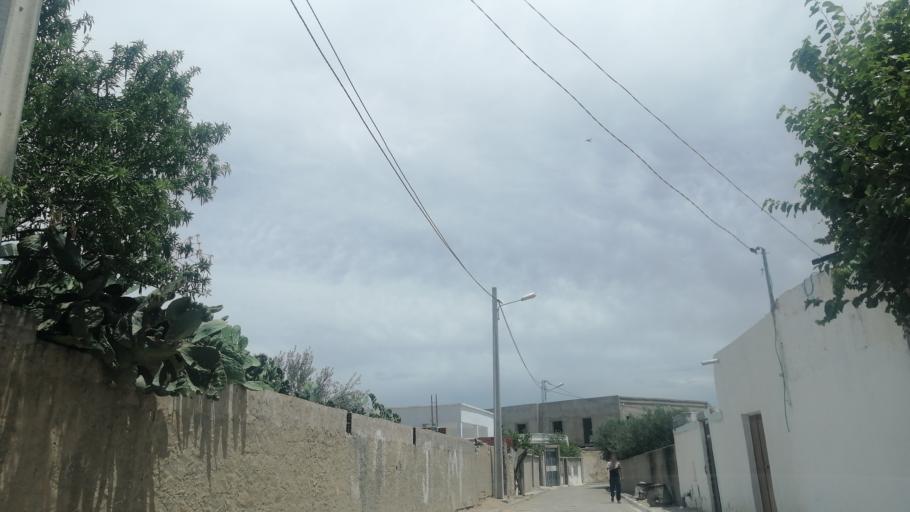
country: TN
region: Al Qayrawan
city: Sbikha
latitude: 36.1280
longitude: 10.0944
